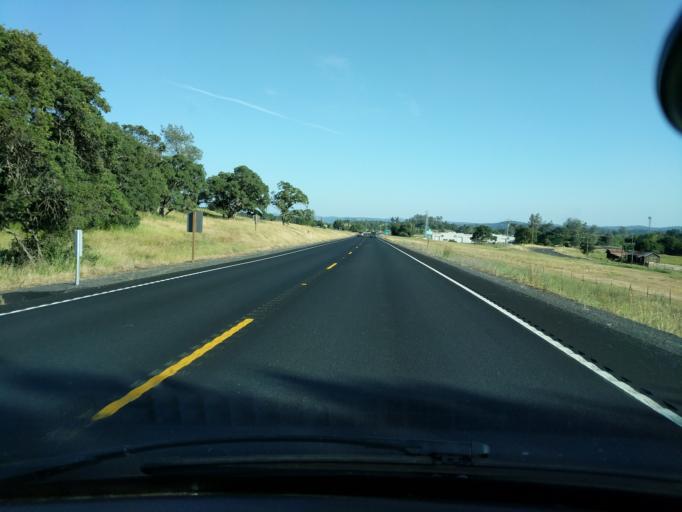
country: US
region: California
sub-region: Calaveras County
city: Copperopolis
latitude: 37.9889
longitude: -120.6486
